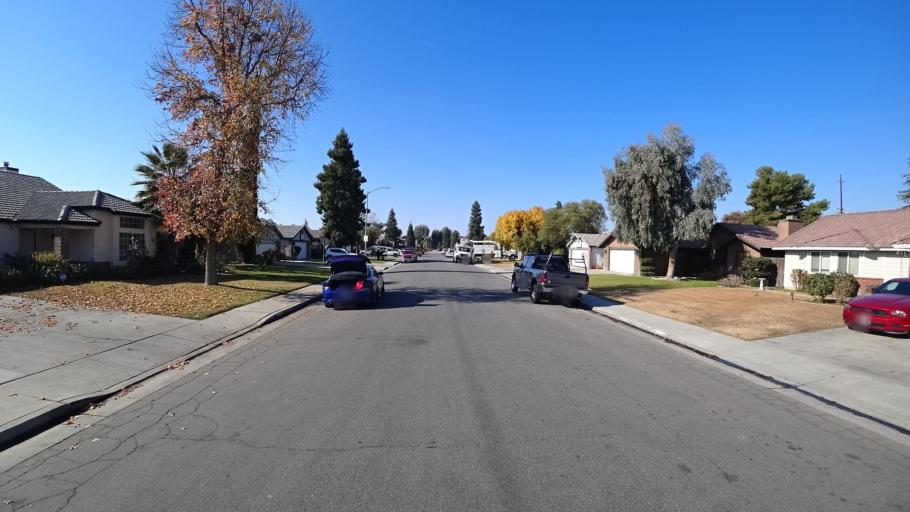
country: US
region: California
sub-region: Kern County
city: Greenfield
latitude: 35.2952
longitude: -119.0490
